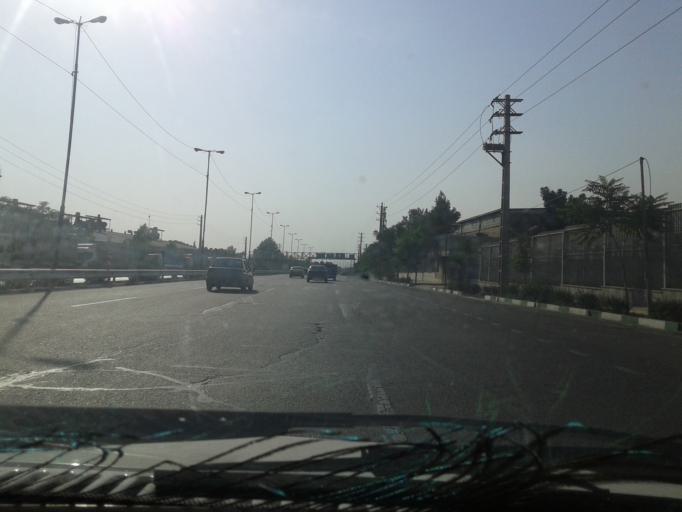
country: IR
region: Tehran
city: Tehran
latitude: 35.7241
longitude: 51.5737
